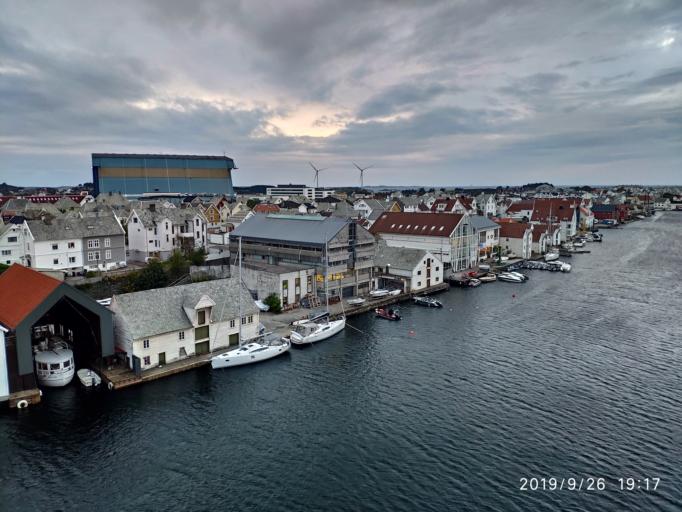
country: NO
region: Rogaland
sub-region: Haugesund
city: Haugesund
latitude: 59.4107
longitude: 5.2696
